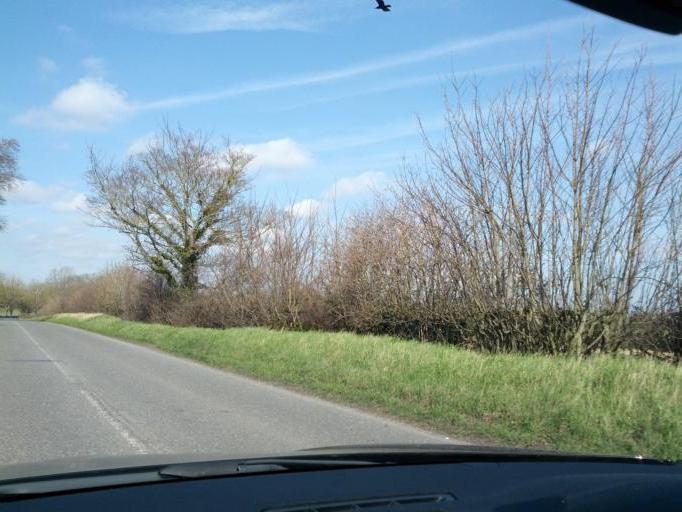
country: IE
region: Leinster
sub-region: Kildare
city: Maynooth
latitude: 53.3959
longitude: -6.6014
